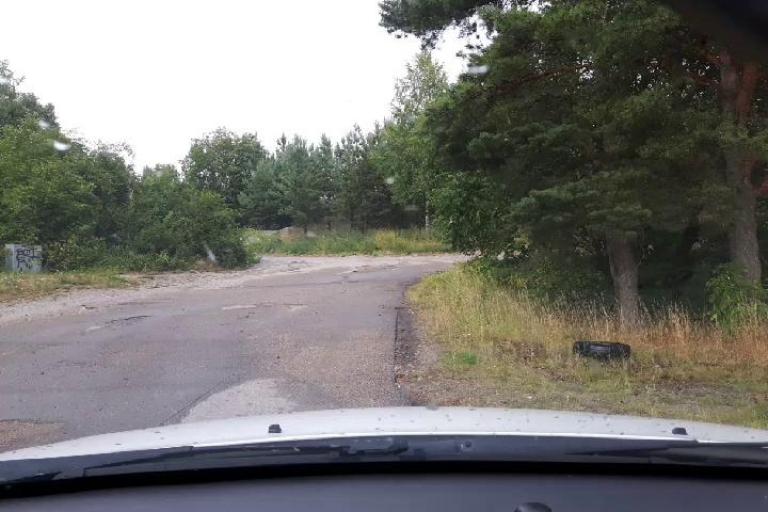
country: SE
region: Uppsala
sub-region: Uppsala Kommun
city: Gamla Uppsala
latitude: 59.8977
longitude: 17.6137
